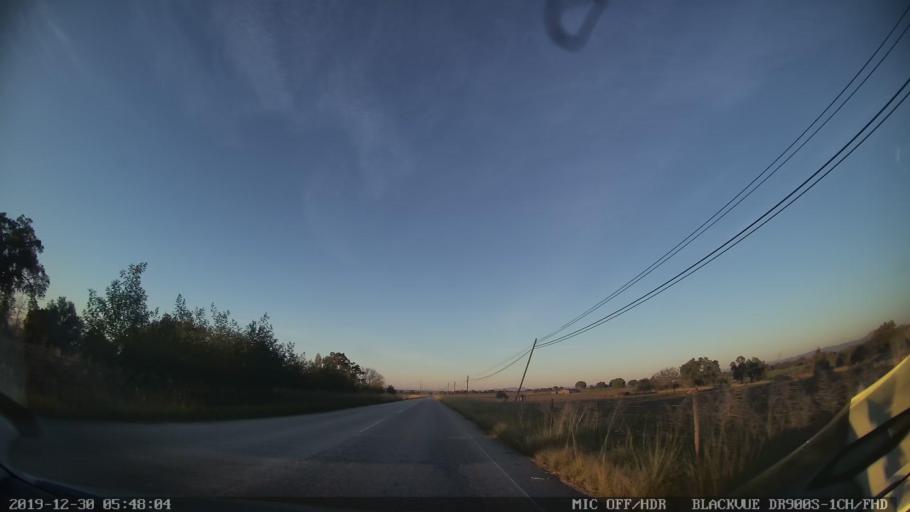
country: PT
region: Castelo Branco
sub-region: Idanha-A-Nova
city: Idanha-a-Nova
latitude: 39.9579
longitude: -7.2417
